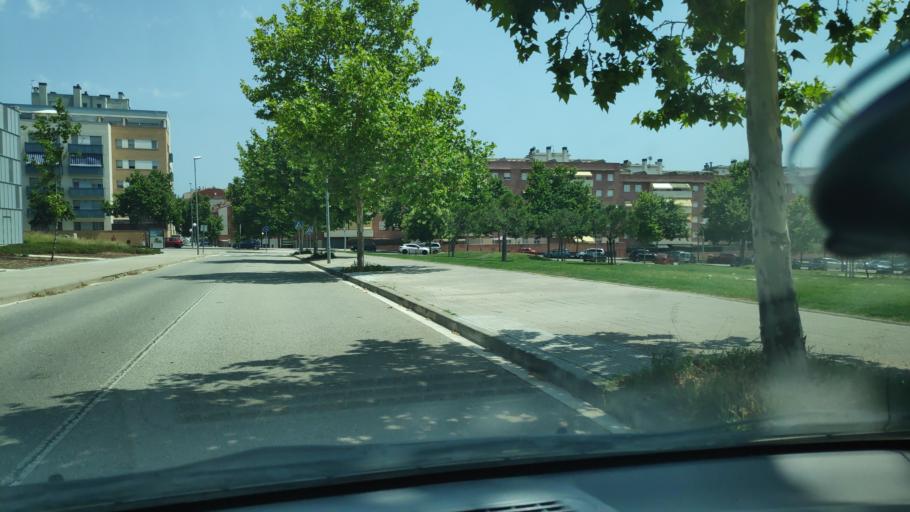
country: ES
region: Catalonia
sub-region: Provincia de Barcelona
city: Terrassa
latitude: 41.5619
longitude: 2.0360
